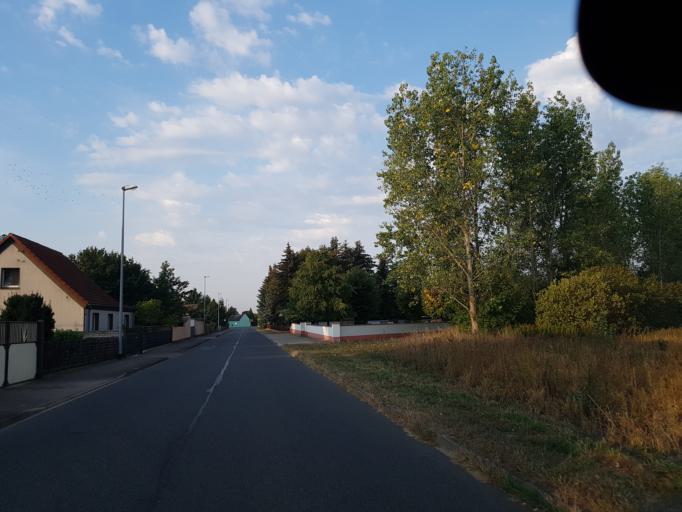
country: DE
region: Brandenburg
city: Hohenleipisch
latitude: 51.4718
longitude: 13.5687
